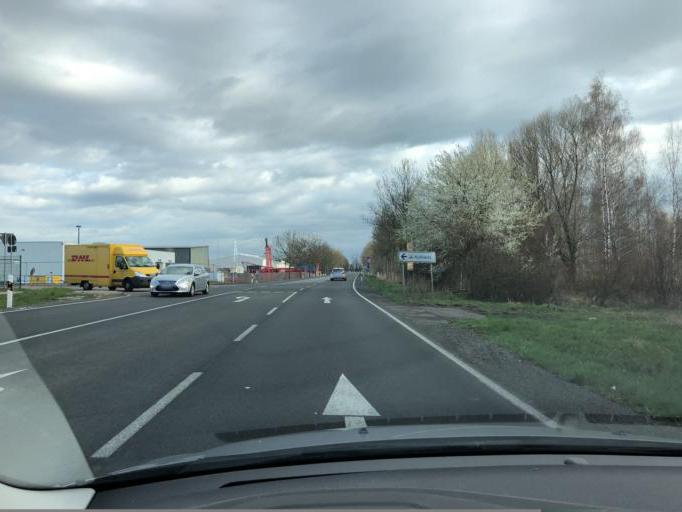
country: DE
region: Saxony
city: Markranstadt
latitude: 51.2868
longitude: 12.2436
